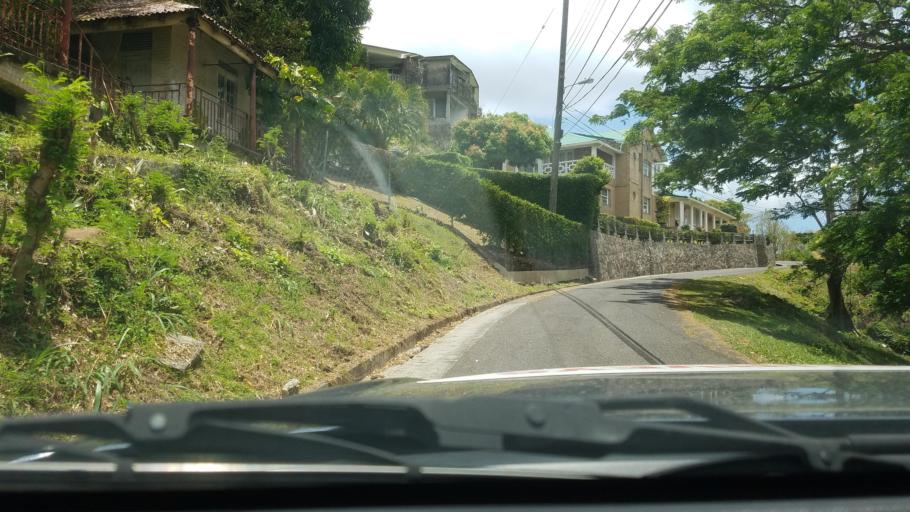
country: LC
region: Castries Quarter
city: Bisee
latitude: 14.0224
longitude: -61.0002
